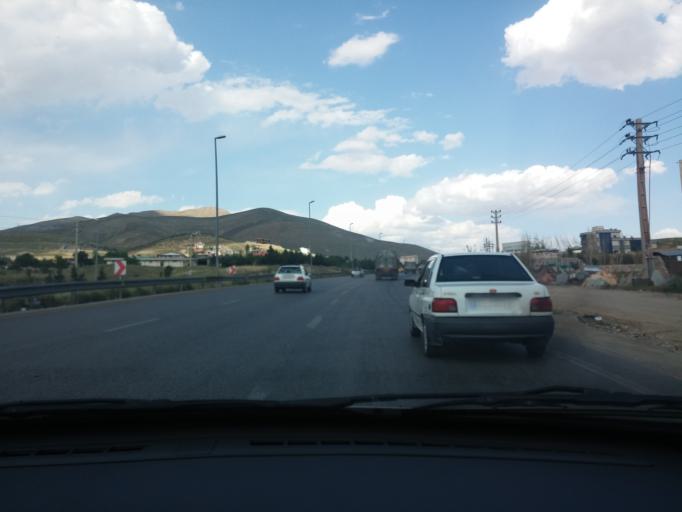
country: IR
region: Tehran
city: Damavand
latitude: 35.7179
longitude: 51.9382
